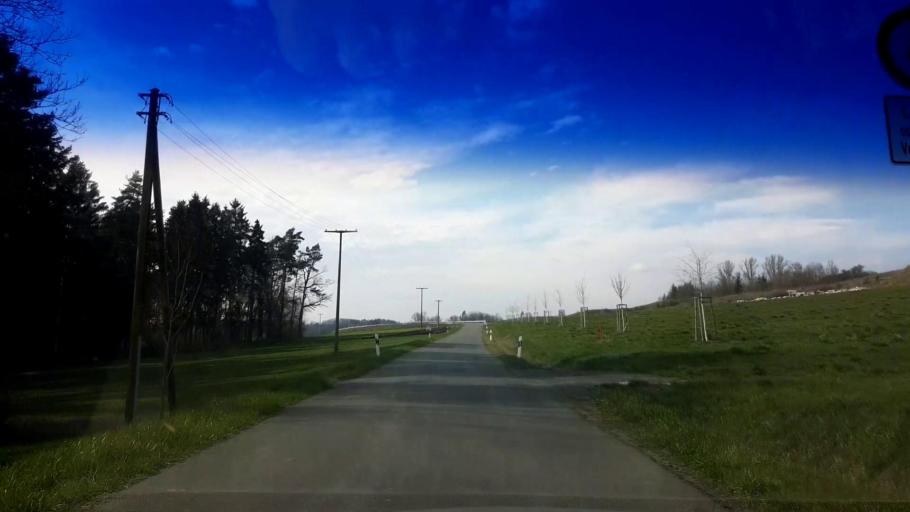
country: DE
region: Bavaria
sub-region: Upper Franconia
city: Harsdorf
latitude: 50.0255
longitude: 11.5930
